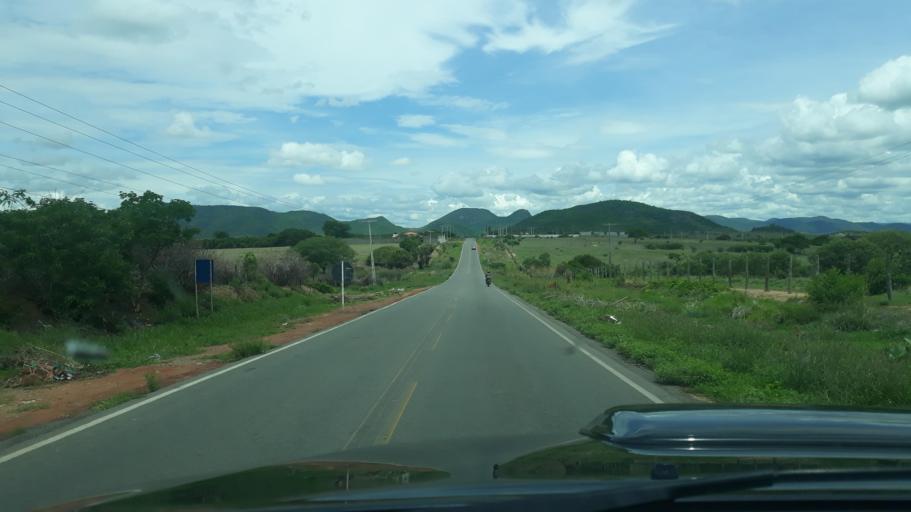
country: BR
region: Bahia
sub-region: Guanambi
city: Guanambi
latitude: -14.2472
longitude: -42.7550
